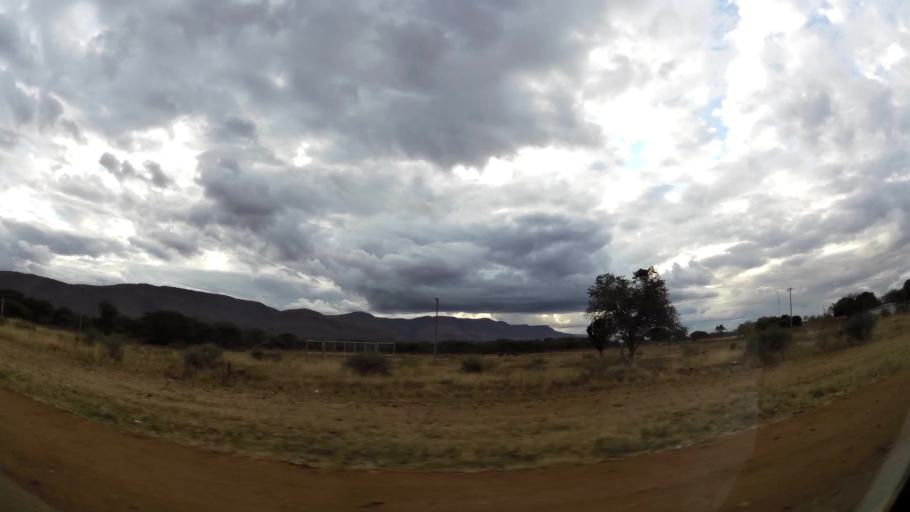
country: ZA
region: Limpopo
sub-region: Waterberg District Municipality
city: Mokopane
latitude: -24.2213
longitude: 29.0038
